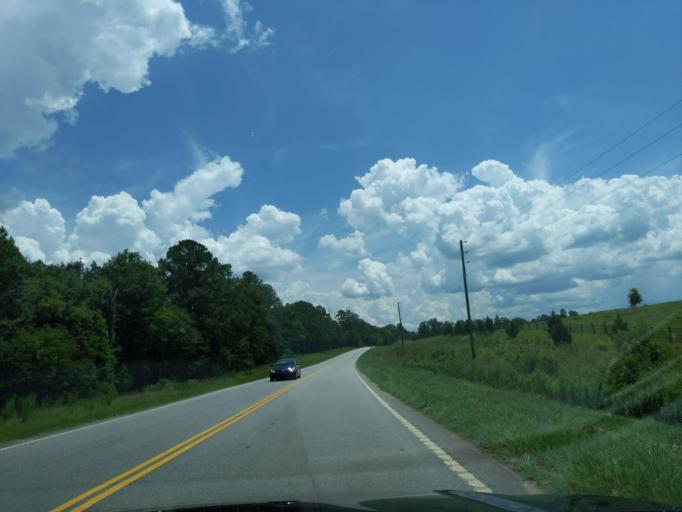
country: US
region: South Carolina
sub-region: Edgefield County
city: Edgefield
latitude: 33.8622
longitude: -81.9858
